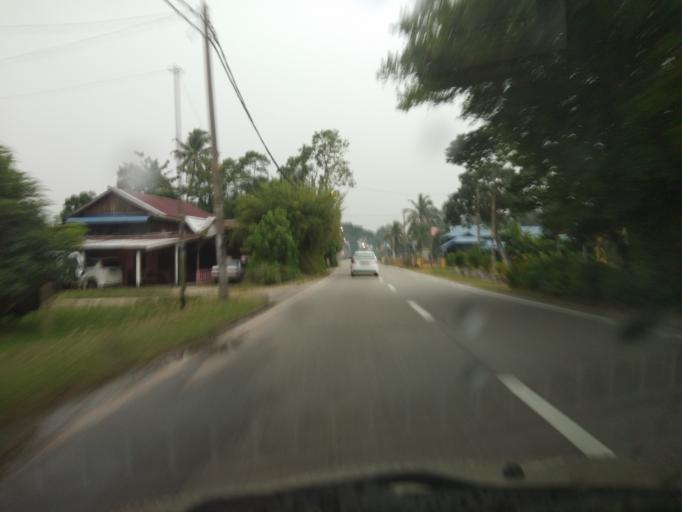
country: MY
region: Penang
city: Permatang Kuching
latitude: 5.4811
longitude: 100.4012
